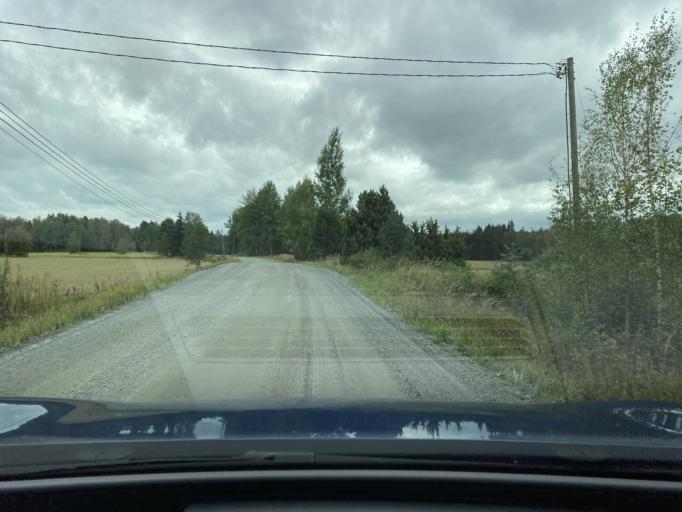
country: FI
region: Pirkanmaa
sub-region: Lounais-Pirkanmaa
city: Vammala
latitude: 61.2676
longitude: 22.9809
